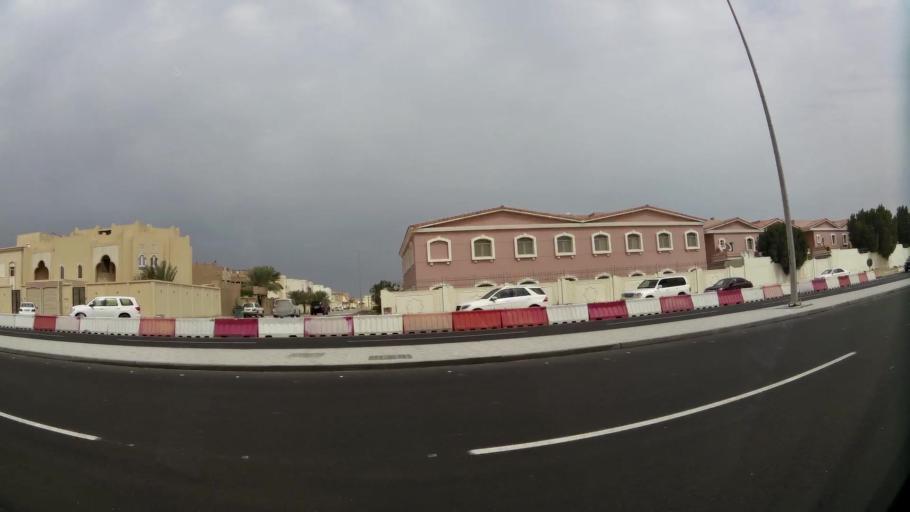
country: QA
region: Baladiyat ar Rayyan
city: Ar Rayyan
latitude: 25.3503
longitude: 51.4660
